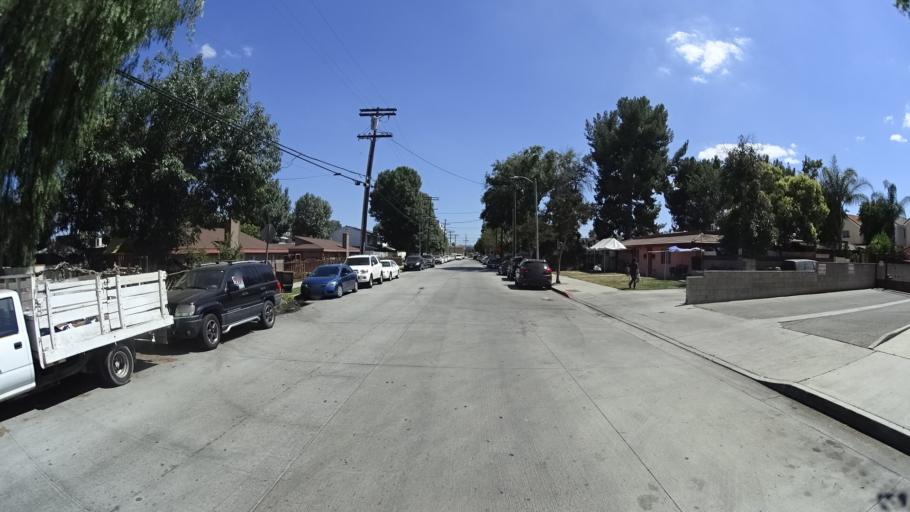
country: US
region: California
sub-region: Los Angeles County
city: Van Nuys
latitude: 34.2238
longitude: -118.4633
